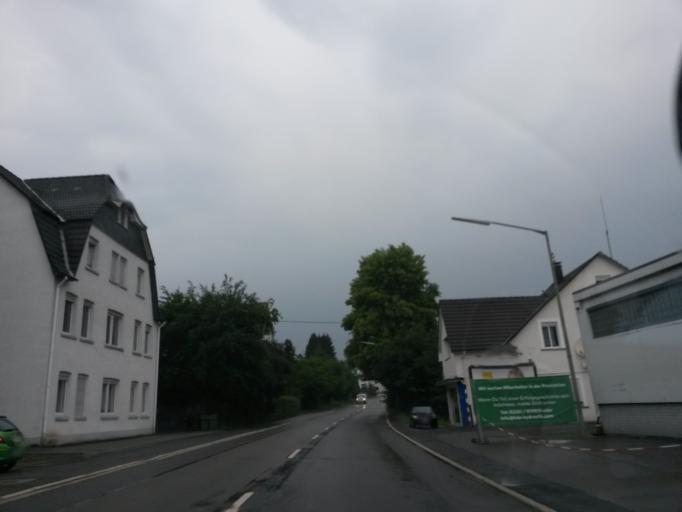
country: DE
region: North Rhine-Westphalia
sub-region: Regierungsbezirk Koln
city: Gummersbach
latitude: 51.0405
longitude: 7.5545
